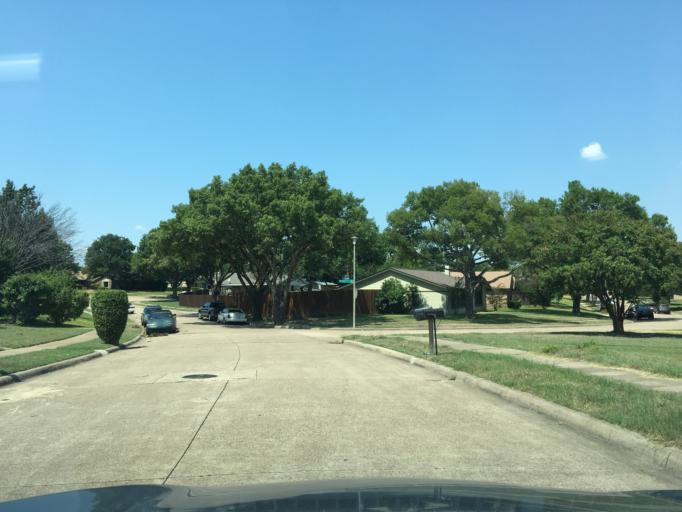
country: US
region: Texas
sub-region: Dallas County
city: Garland
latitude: 32.9625
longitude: -96.6674
